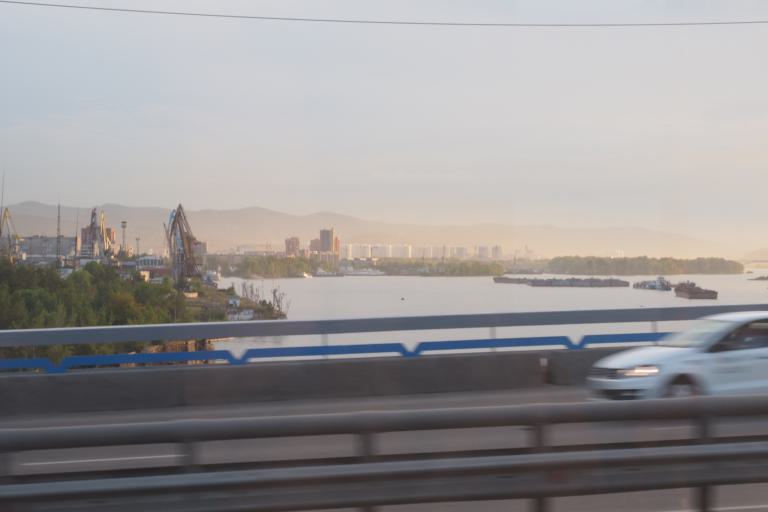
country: RU
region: Krasnoyarskiy
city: Krasnoyarsk
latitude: 56.0174
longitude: 92.9543
